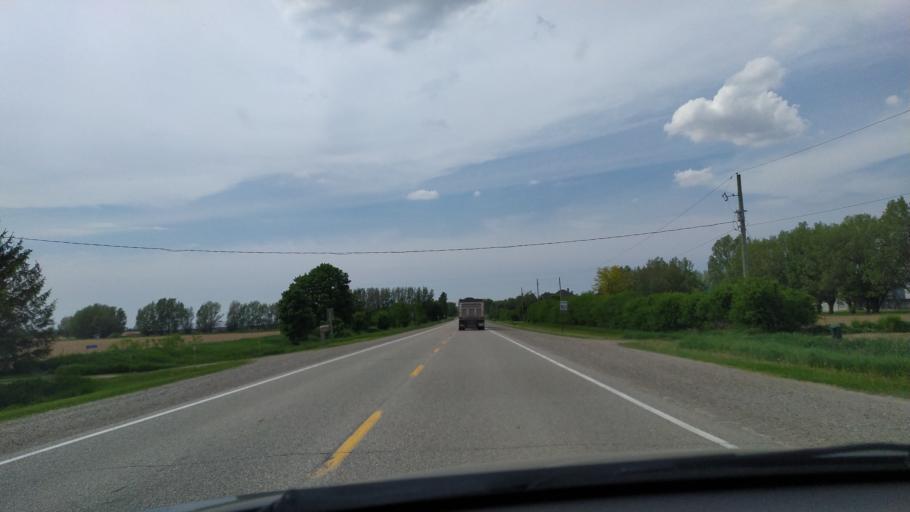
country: CA
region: Ontario
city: Stratford
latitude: 43.2222
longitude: -81.0720
